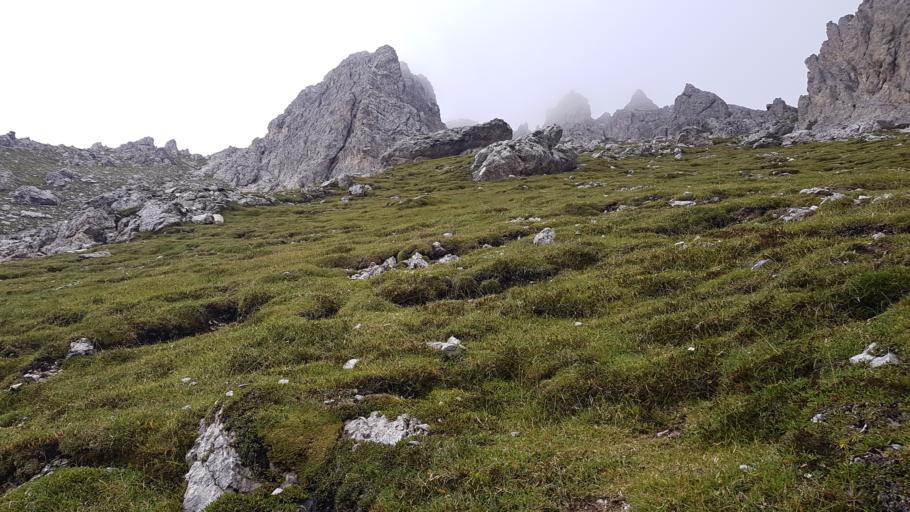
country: IT
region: Veneto
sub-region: Provincia di Belluno
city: San Nicolo Comelico
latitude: 46.6272
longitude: 12.5636
